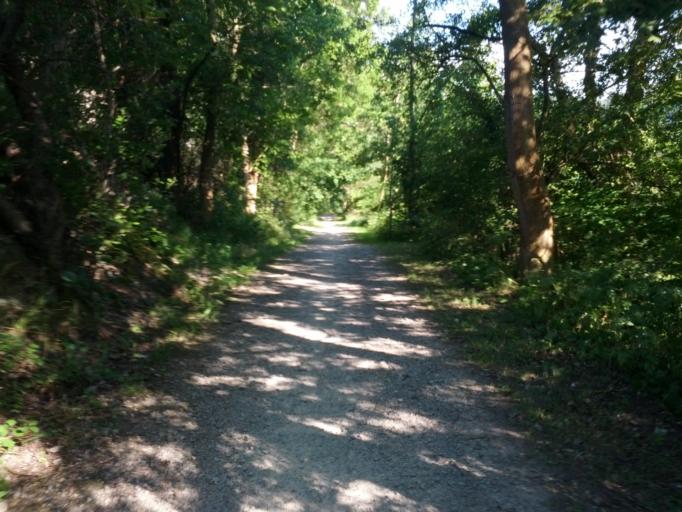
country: DE
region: Thuringia
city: Creuzburg
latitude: 51.0659
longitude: 10.2696
